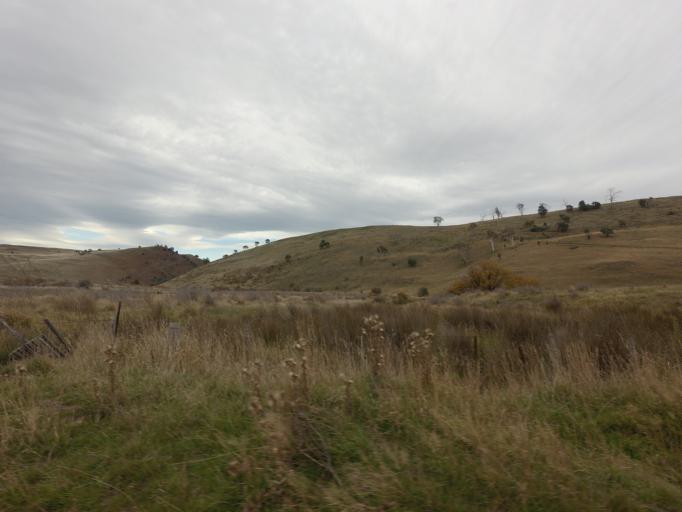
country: AU
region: Tasmania
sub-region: Derwent Valley
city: New Norfolk
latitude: -42.3673
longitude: 146.8428
